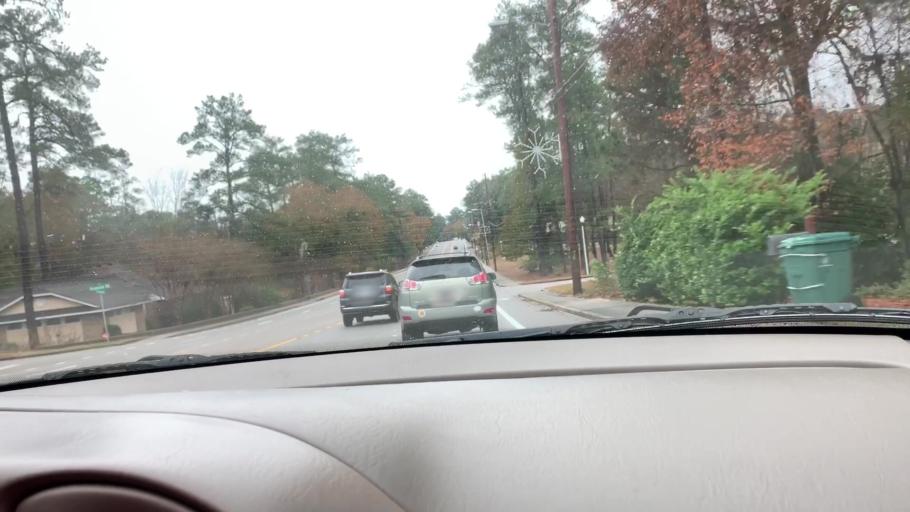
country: US
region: South Carolina
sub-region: Richland County
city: Dentsville
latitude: 34.0353
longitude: -80.9646
